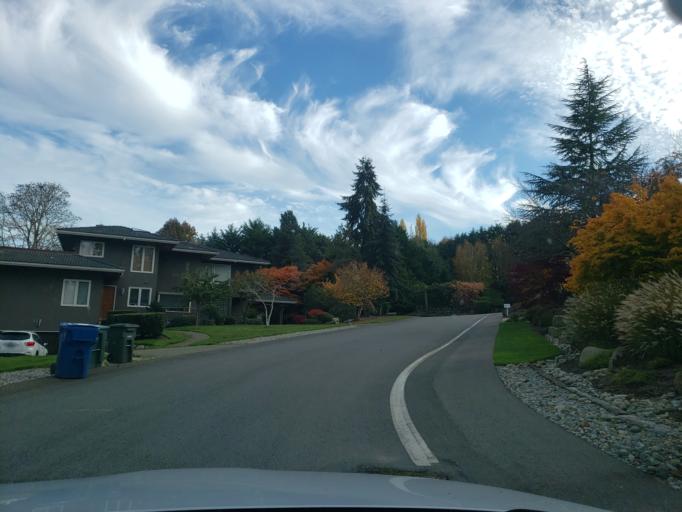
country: US
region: Washington
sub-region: Snohomish County
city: Woodway
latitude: 47.8010
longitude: -122.3867
